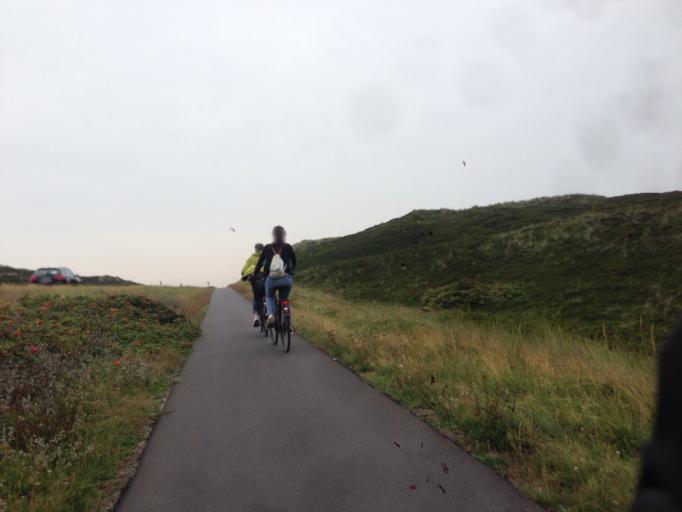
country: DE
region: Schleswig-Holstein
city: Westerland
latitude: 54.7969
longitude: 8.2882
